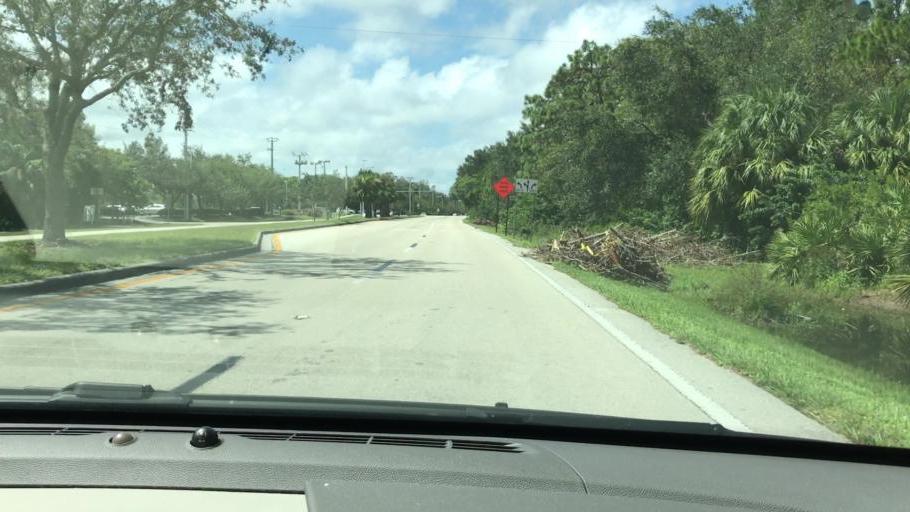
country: US
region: Florida
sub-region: Lee County
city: Estero
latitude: 26.4313
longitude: -81.8082
